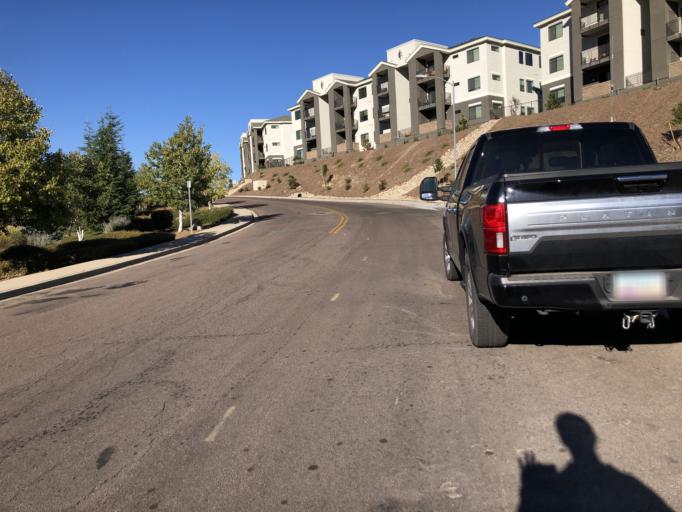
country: US
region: Arizona
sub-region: Yavapai County
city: Prescott
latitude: 34.5497
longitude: -112.4008
